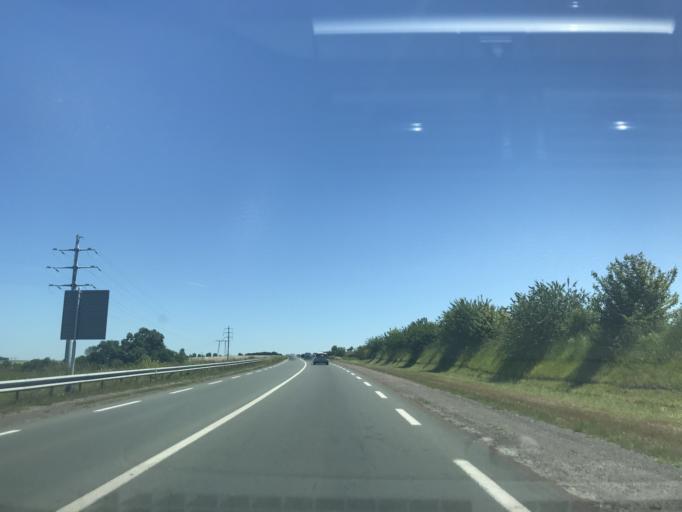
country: FR
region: Poitou-Charentes
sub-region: Departement de la Charente-Maritime
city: Saint-Georges-de-Didonne
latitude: 45.6148
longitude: -0.9859
